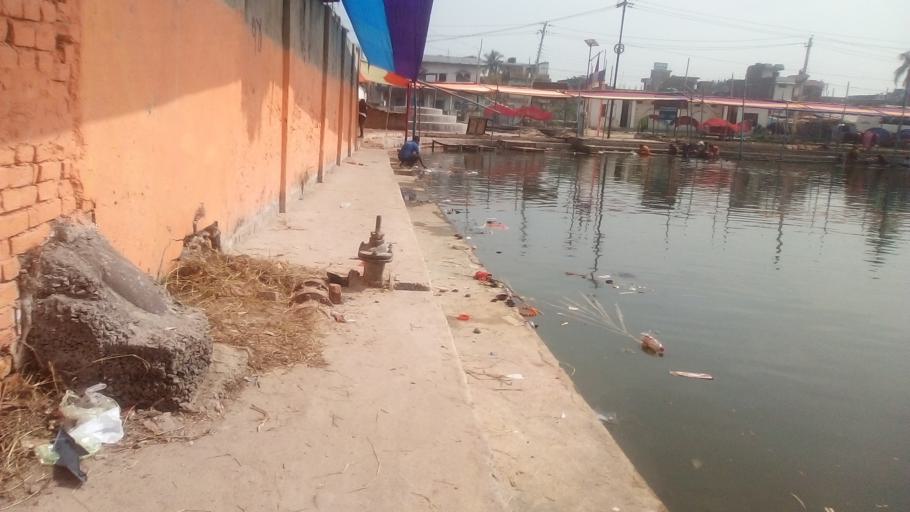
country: NP
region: Central Region
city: Janakpur
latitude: 26.7328
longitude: 85.9255
